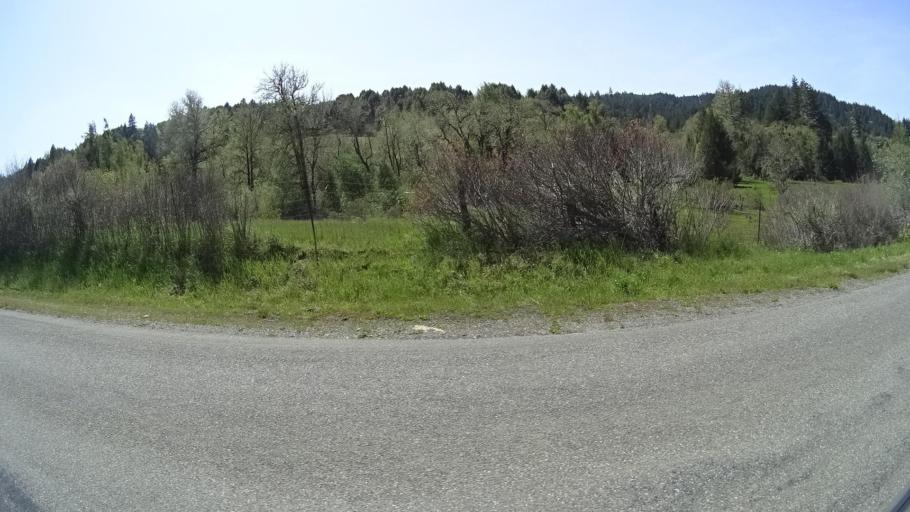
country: US
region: California
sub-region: Humboldt County
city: Redway
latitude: 40.2974
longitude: -123.6522
